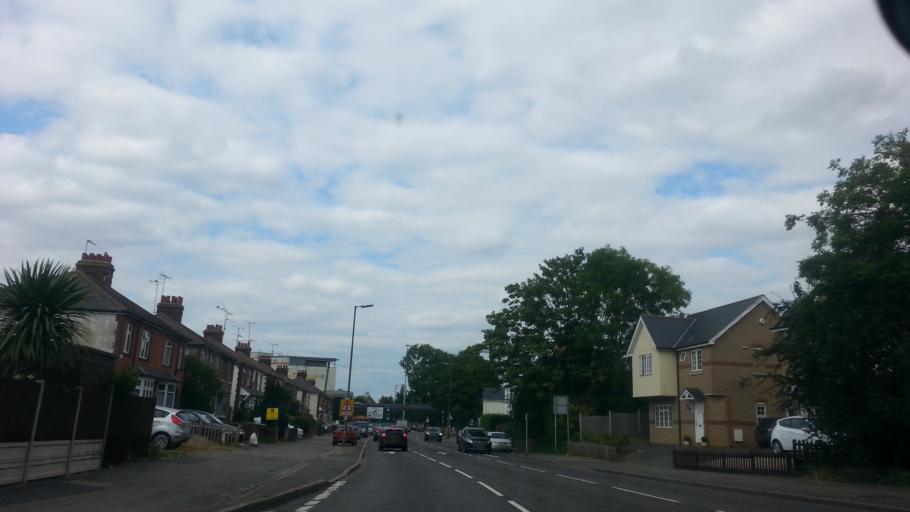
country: GB
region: England
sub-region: Essex
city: Chelmsford
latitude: 51.7249
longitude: 0.4801
